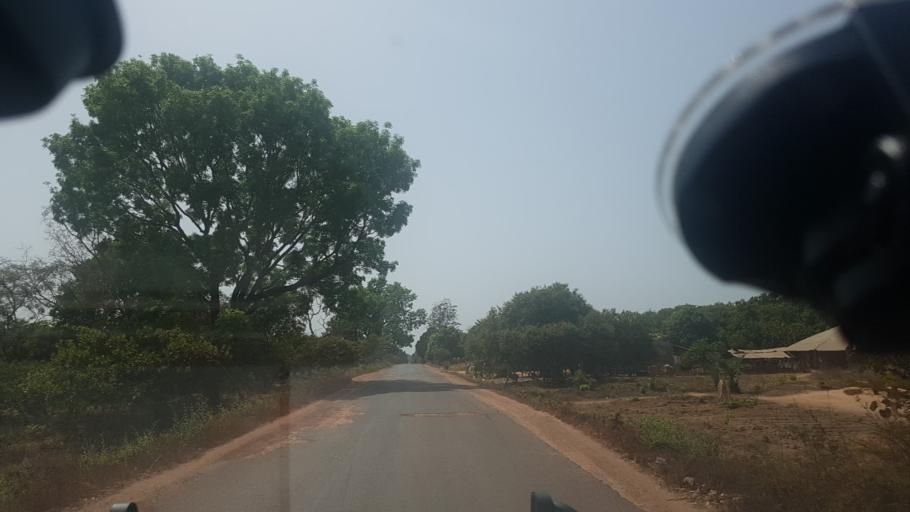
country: GW
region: Cacheu
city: Cacheu
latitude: 12.4095
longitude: -16.0442
